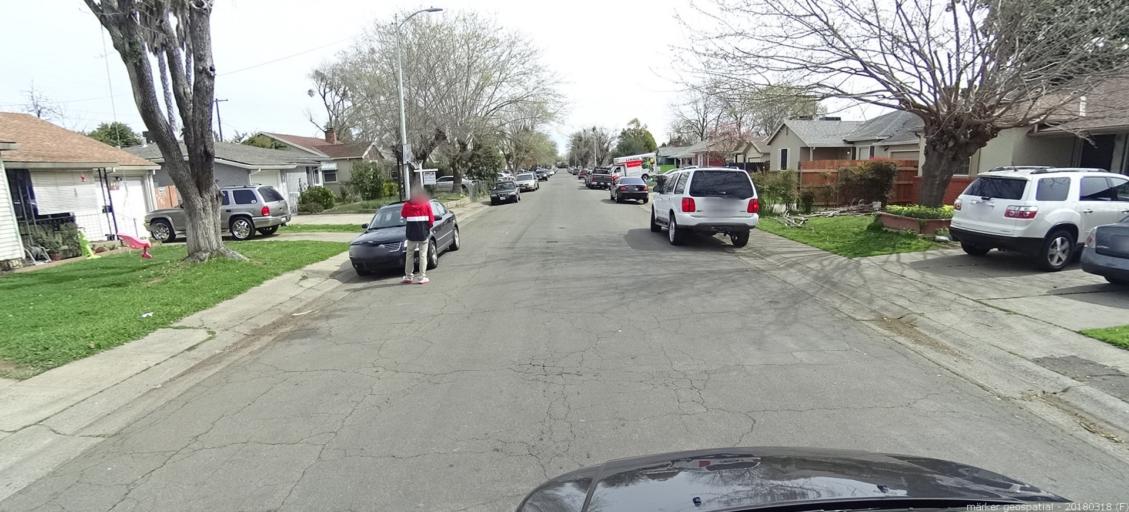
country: US
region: California
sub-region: Sacramento County
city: Parkway
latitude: 38.5173
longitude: -121.4548
